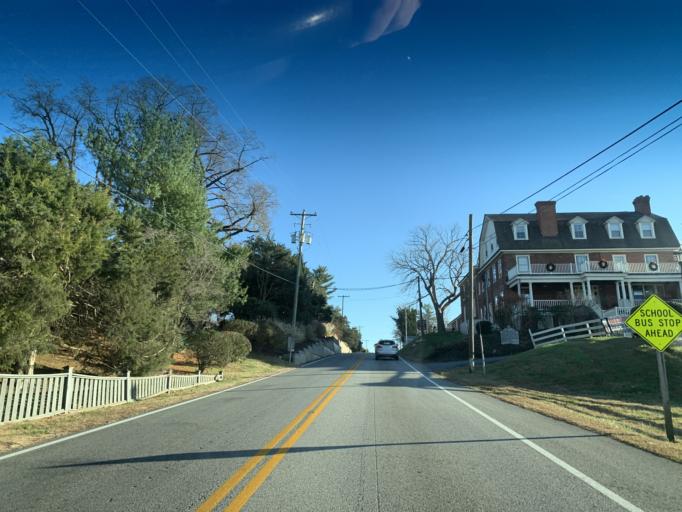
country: US
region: Delaware
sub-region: New Castle County
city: Middletown
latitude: 39.3615
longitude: -75.8803
